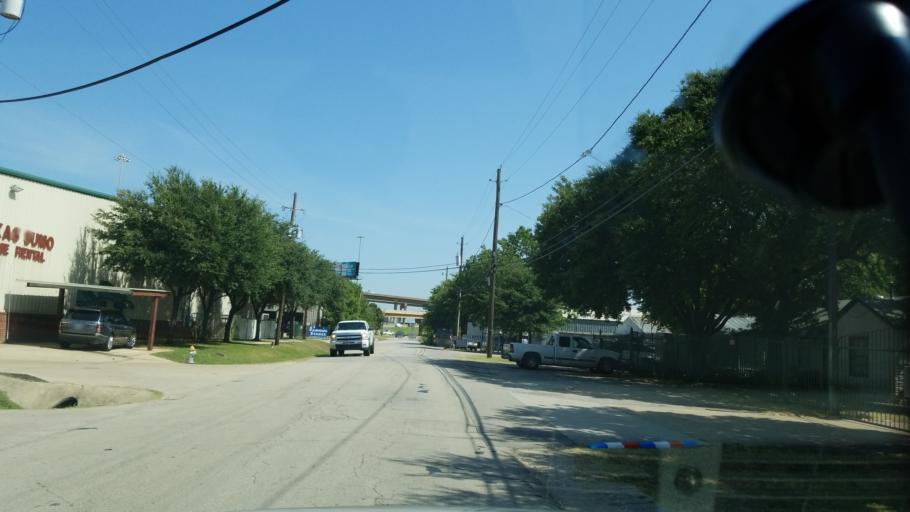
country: US
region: Texas
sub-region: Dallas County
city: Farmers Branch
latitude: 32.9035
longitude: -96.8958
